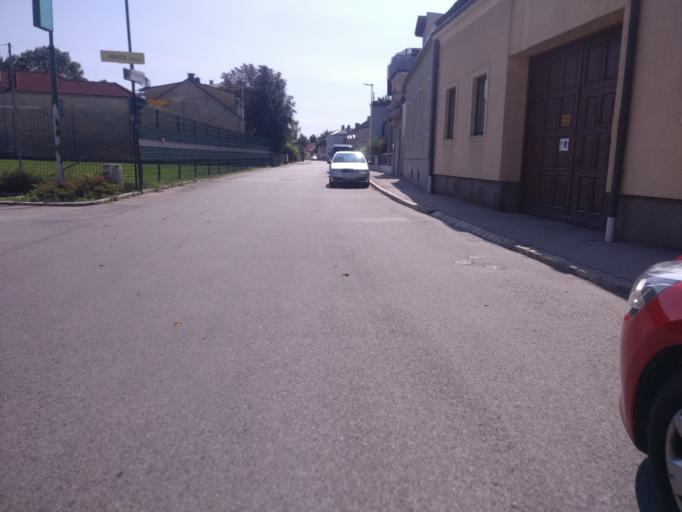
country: AT
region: Lower Austria
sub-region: Politischer Bezirk Modling
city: Guntramsdorf
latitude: 48.0461
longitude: 16.3131
